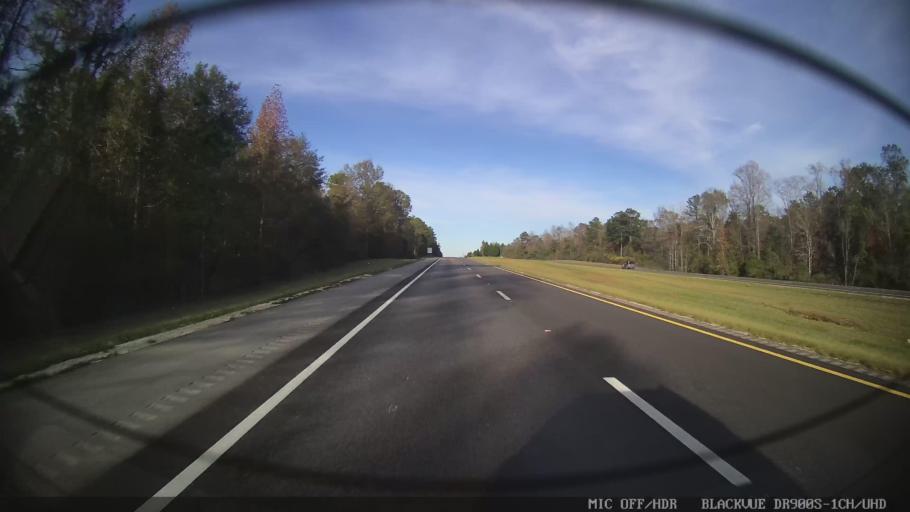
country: US
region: Mississippi
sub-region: Lamar County
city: Purvis
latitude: 31.1532
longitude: -89.3614
